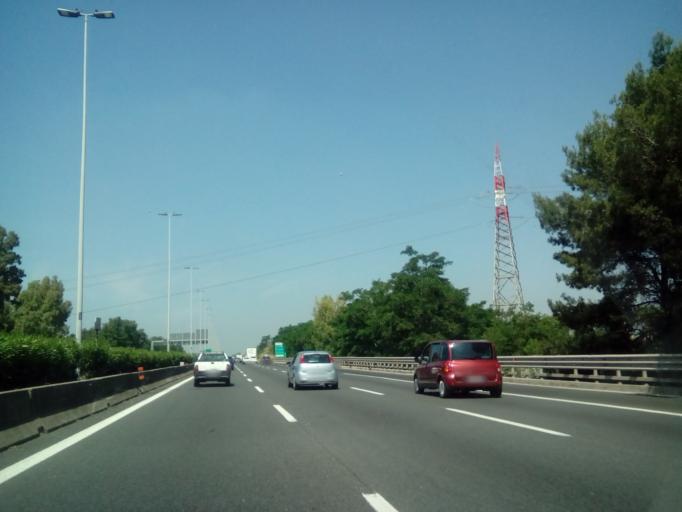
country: IT
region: Latium
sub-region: Citta metropolitana di Roma Capitale
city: Selcetta
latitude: 41.7981
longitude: 12.4772
